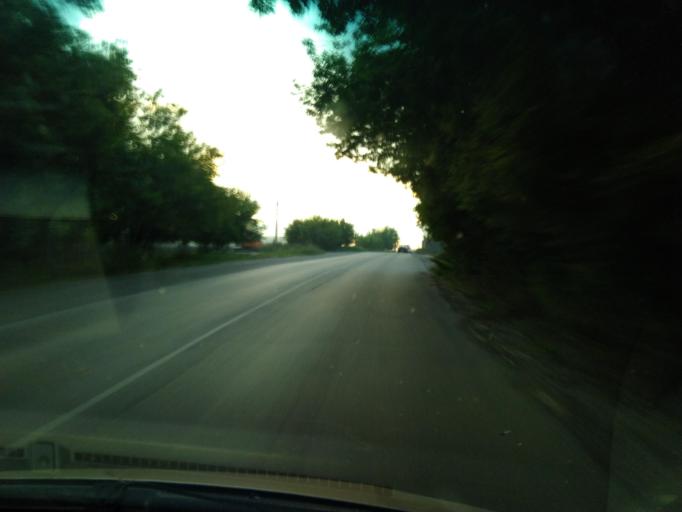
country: RU
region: Krasnoyarskiy
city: Krasnoyarsk
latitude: 55.9637
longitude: 92.9892
